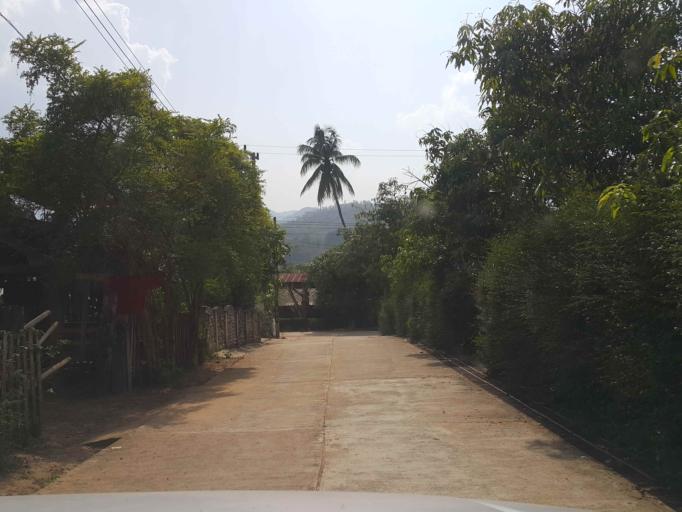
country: TH
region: Chiang Mai
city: Wiang Haeng
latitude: 19.3954
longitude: 98.7226
